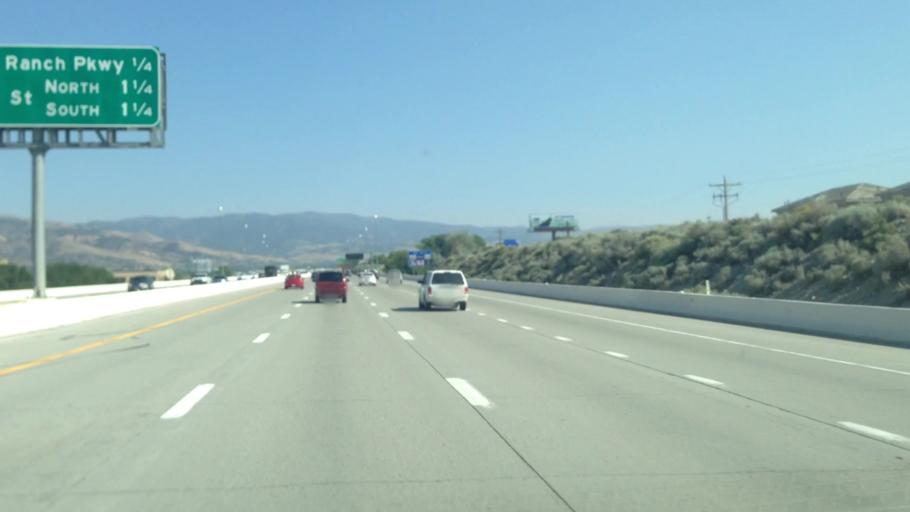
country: US
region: Nevada
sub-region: Washoe County
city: Sparks
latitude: 39.4310
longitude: -119.7594
